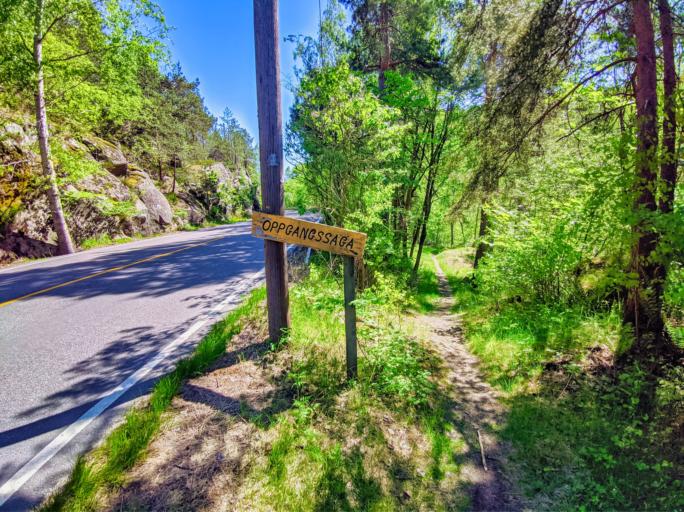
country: NO
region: Akershus
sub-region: Oppegard
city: Kolbotn
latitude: 59.8283
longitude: 10.7685
